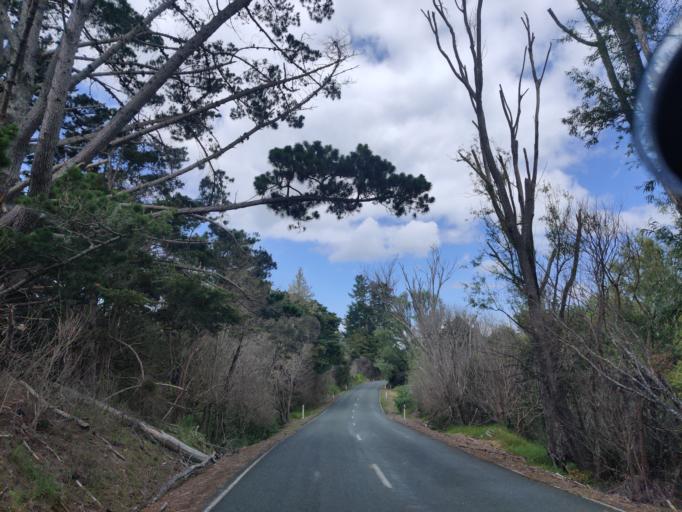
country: NZ
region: Northland
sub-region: Far North District
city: Kaitaia
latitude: -35.2799
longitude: 173.4843
